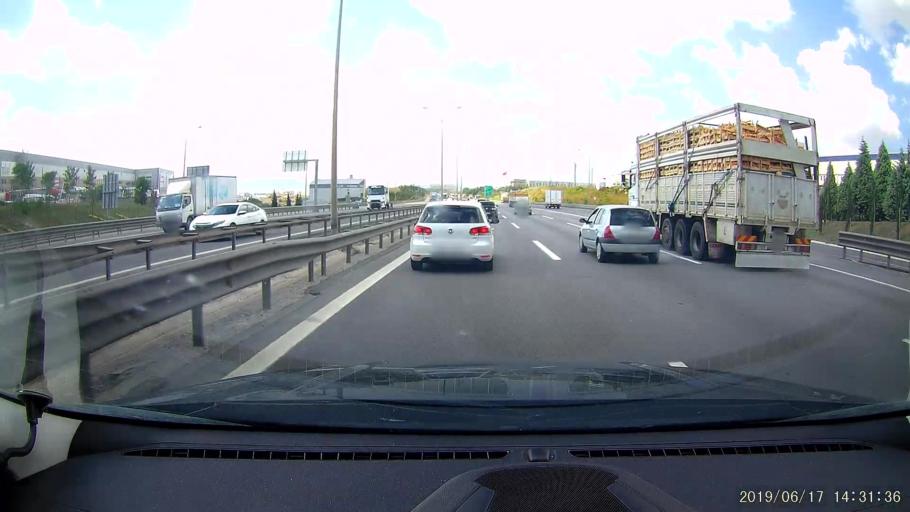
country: TR
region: Kocaeli
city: Balcik
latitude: 40.8556
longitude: 29.4085
